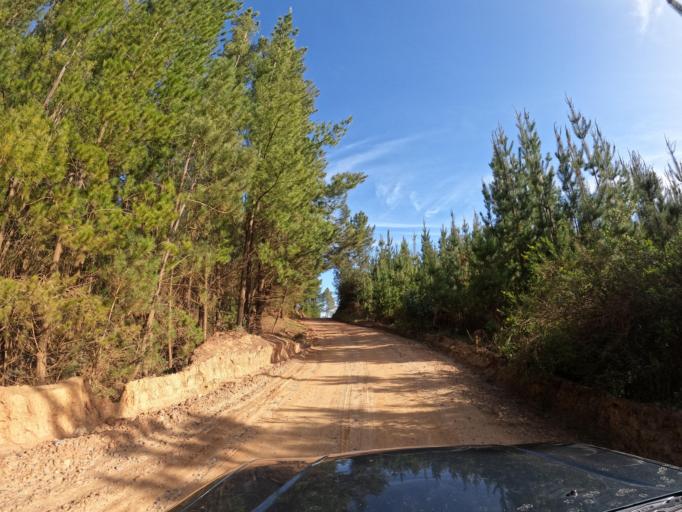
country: CL
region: Biobio
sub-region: Provincia de Biobio
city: Yumbel
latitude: -37.1048
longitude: -72.7418
